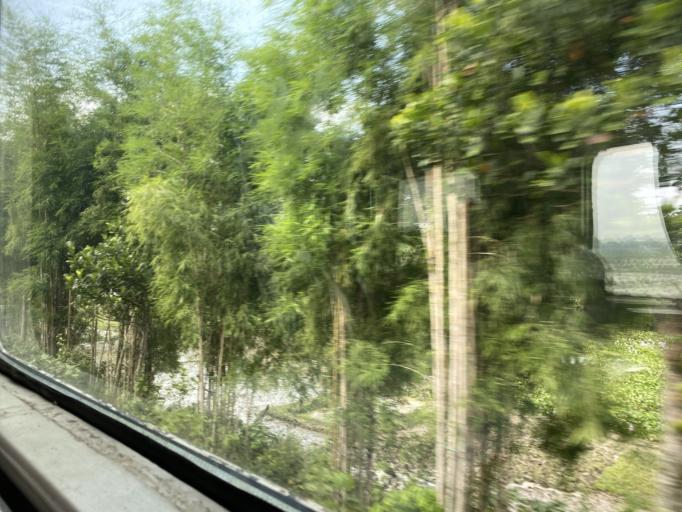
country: IN
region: Tripura
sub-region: West Tripura
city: Agartala
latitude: 23.9958
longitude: 91.2882
